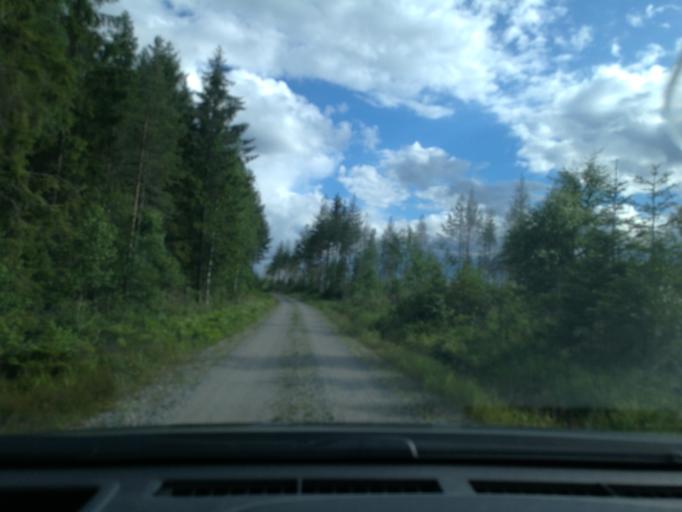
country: SE
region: Vaestmanland
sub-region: Surahammars Kommun
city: Ramnas
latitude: 59.8481
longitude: 16.2785
